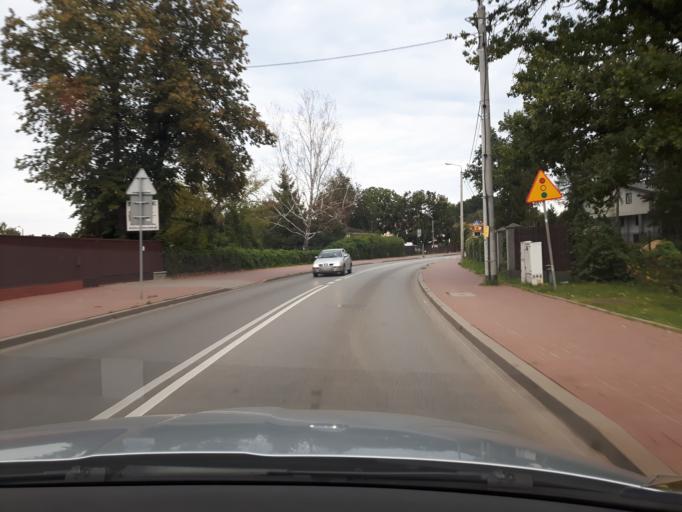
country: PL
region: Masovian Voivodeship
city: Zielonka
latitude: 52.3121
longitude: 21.1494
